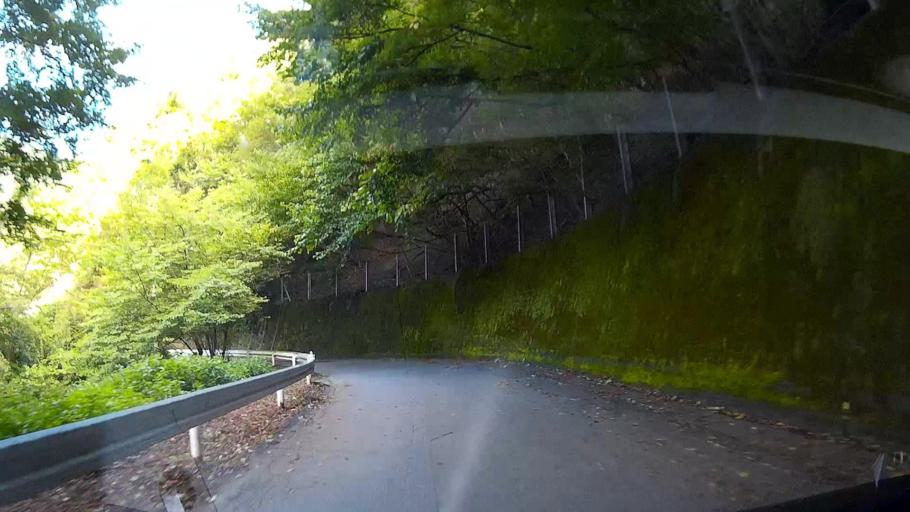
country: JP
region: Shizuoka
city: Shizuoka-shi
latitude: 35.2944
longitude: 138.2176
